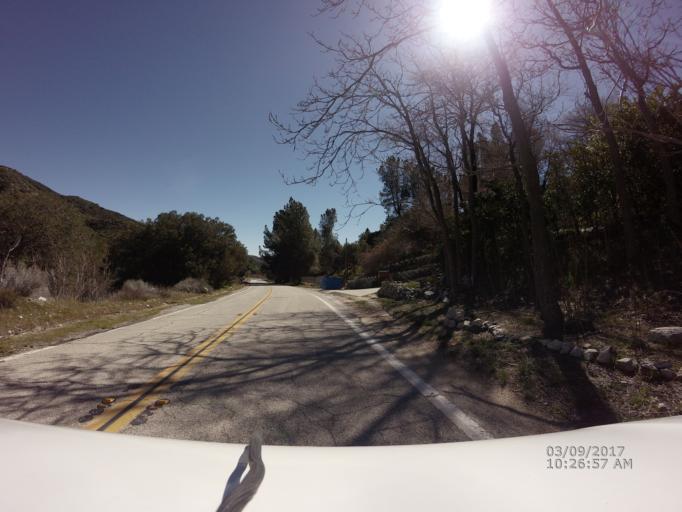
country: US
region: California
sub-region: Los Angeles County
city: Green Valley
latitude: 34.6963
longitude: -118.5016
